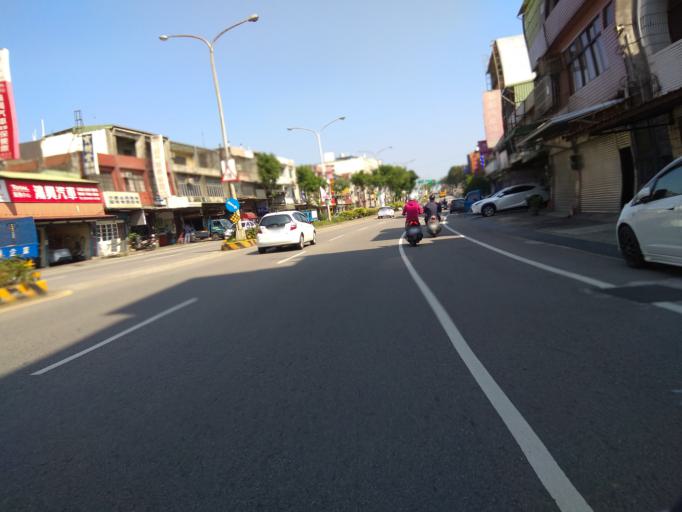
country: TW
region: Taiwan
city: Daxi
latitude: 24.9249
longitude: 121.1889
